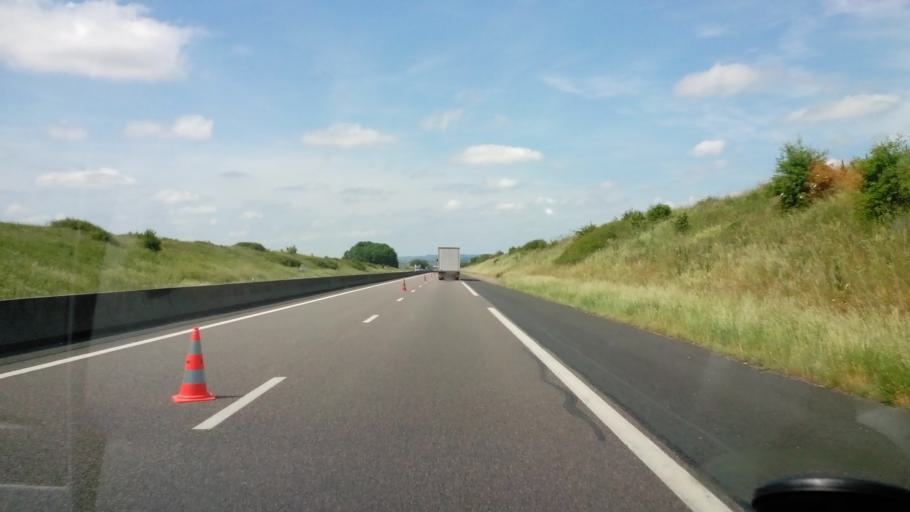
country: FR
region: Lorraine
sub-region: Departement des Vosges
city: Bulgneville
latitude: 48.2259
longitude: 5.8513
